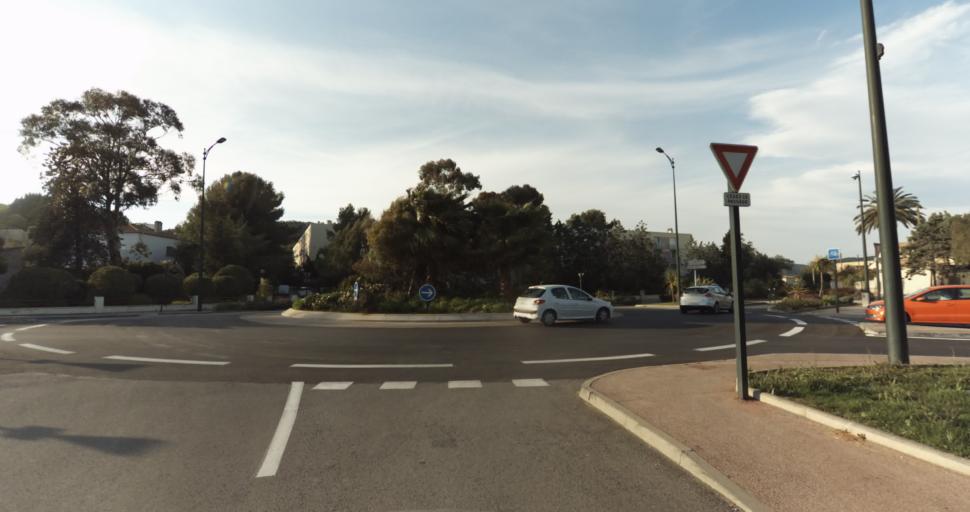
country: FR
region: Provence-Alpes-Cote d'Azur
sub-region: Departement du Var
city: Hyeres
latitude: 43.1246
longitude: 6.1503
